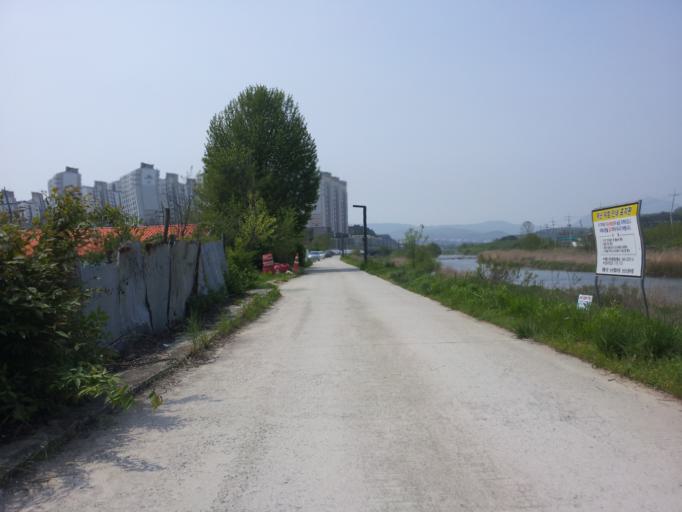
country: KR
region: Daejeon
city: Daejeon
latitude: 36.2672
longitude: 127.2767
